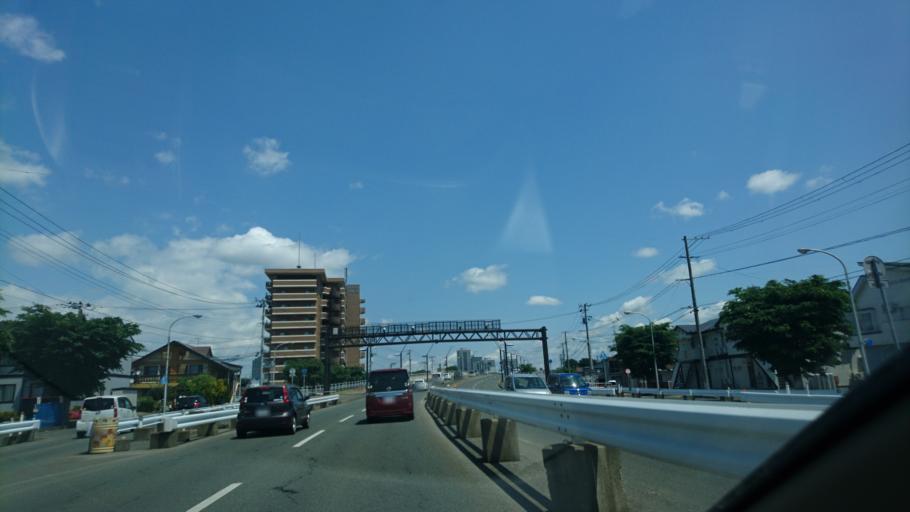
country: JP
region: Iwate
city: Morioka-shi
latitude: 39.6893
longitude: 141.1357
